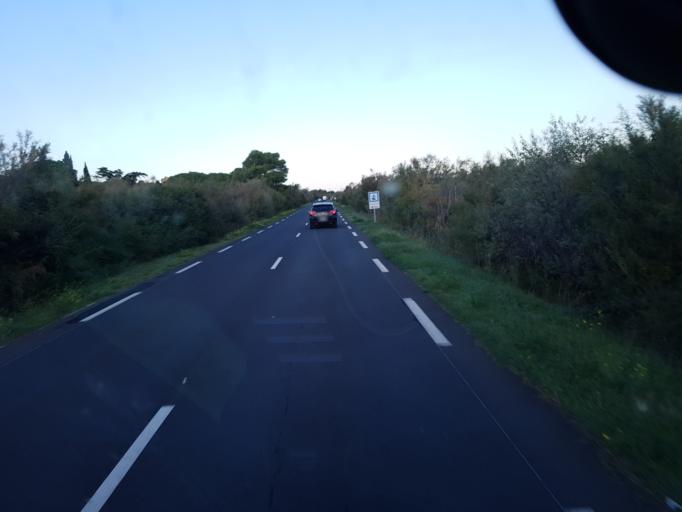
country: FR
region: Languedoc-Roussillon
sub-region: Departement de l'Aude
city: Port-la-Nouvelle
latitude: 42.9837
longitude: 3.0270
